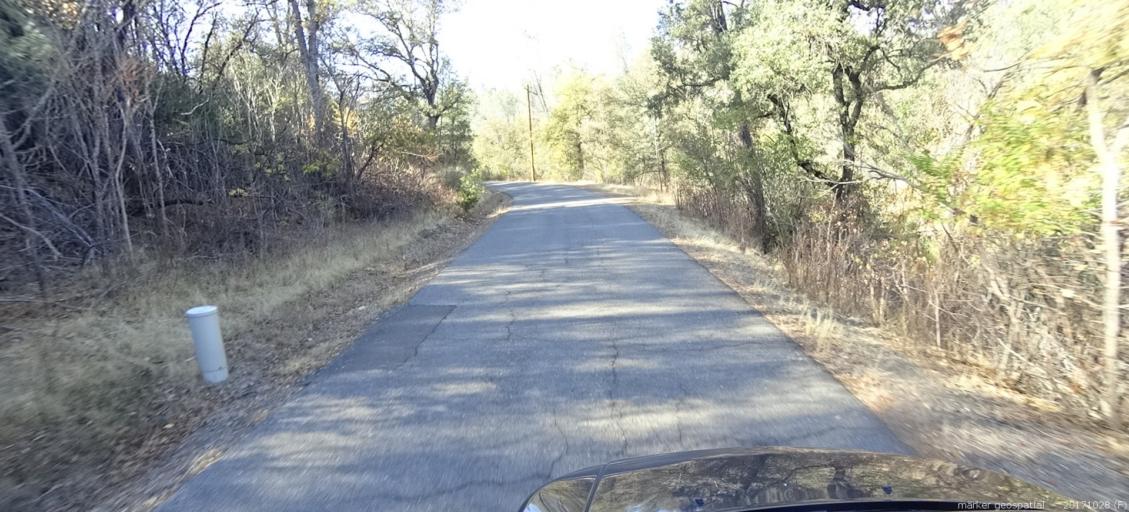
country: US
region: California
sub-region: Shasta County
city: Shasta
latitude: 40.5958
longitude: -122.4479
